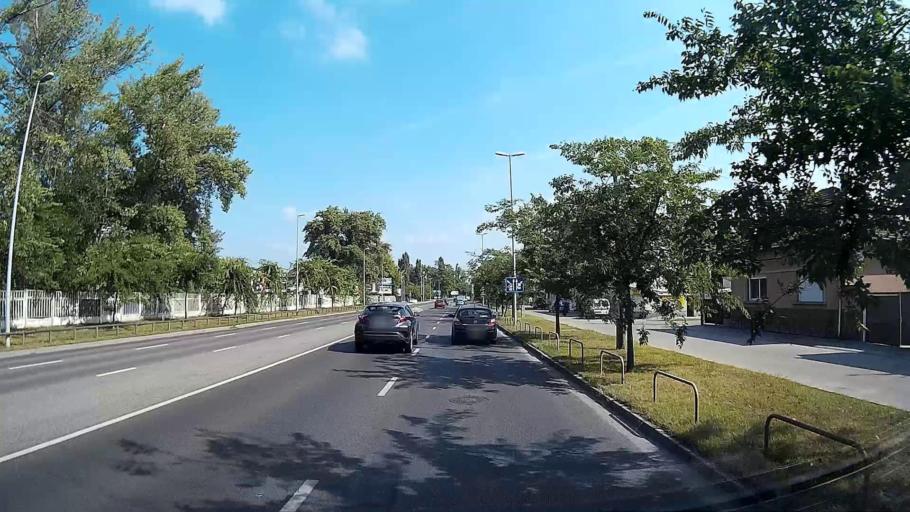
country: HU
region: Budapest
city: Budapest IV. keruelet
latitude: 47.5866
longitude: 19.0821
